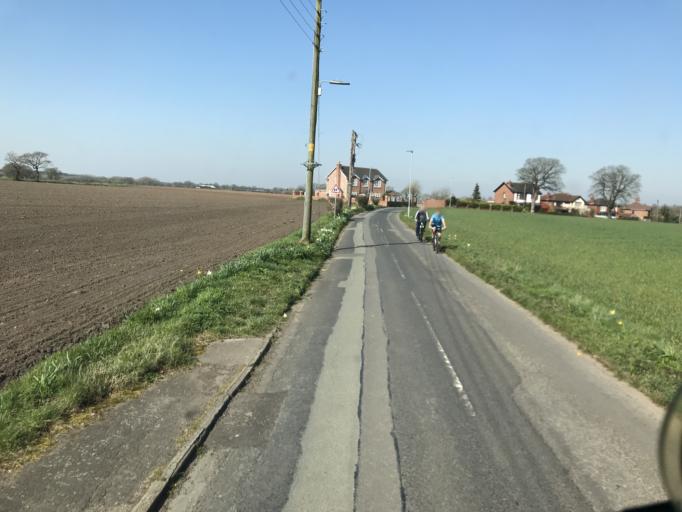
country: GB
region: England
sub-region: Trafford
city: Partington
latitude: 53.4171
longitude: -2.4588
